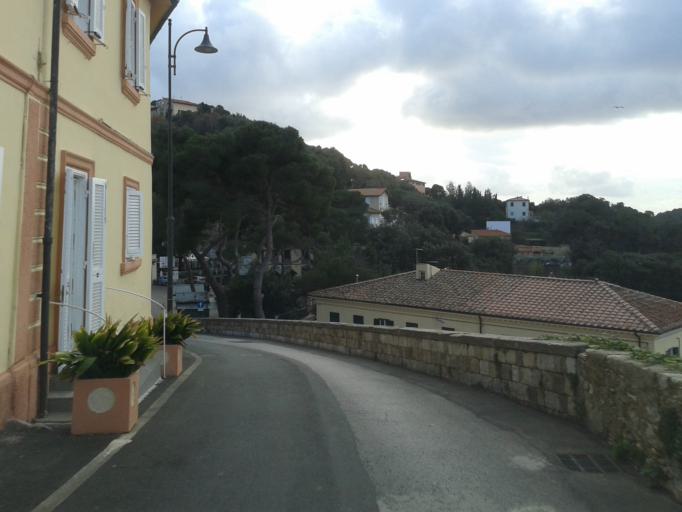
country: IT
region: Tuscany
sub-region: Provincia di Livorno
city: Quercianella
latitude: 43.4937
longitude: 10.3497
